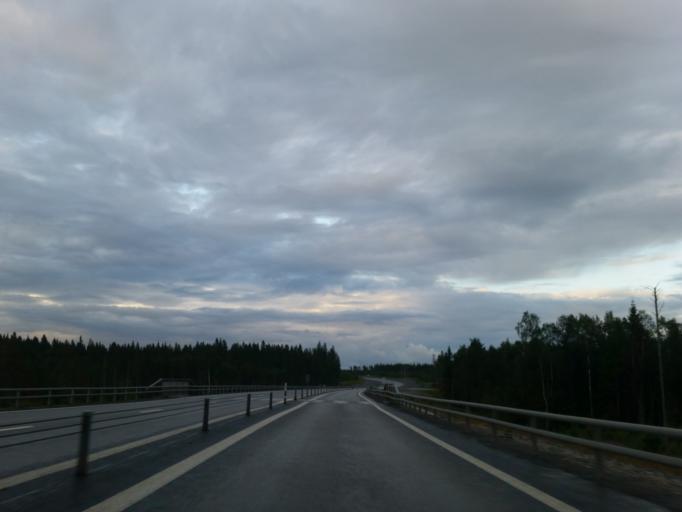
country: SE
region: Vaesterbotten
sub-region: Umea Kommun
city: Umea
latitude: 63.8573
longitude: 20.2507
